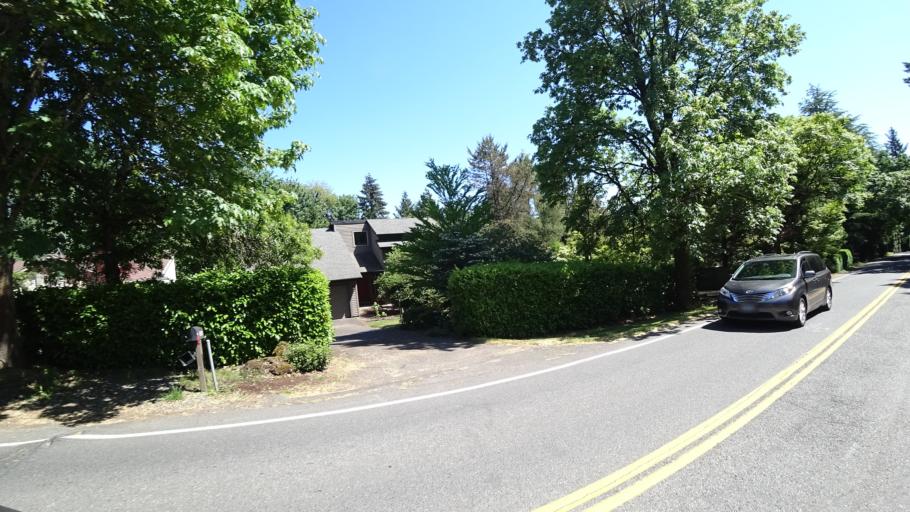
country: US
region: Oregon
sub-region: Washington County
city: Raleigh Hills
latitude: 45.4928
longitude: -122.7278
